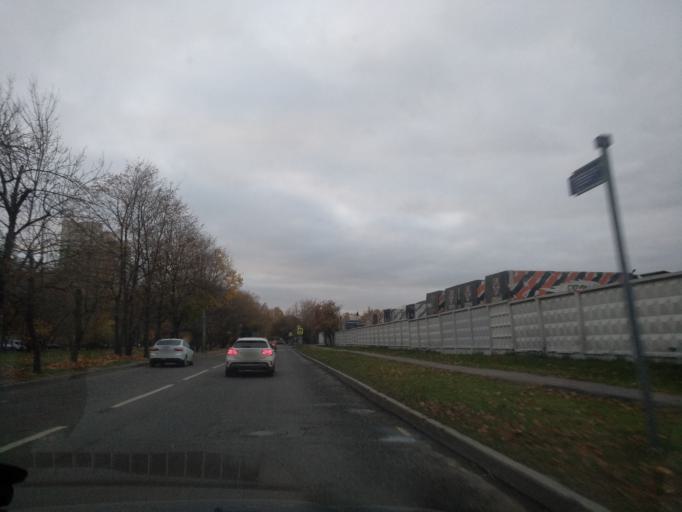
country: RU
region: Moscow
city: Kozeyevo
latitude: 55.8793
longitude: 37.6311
